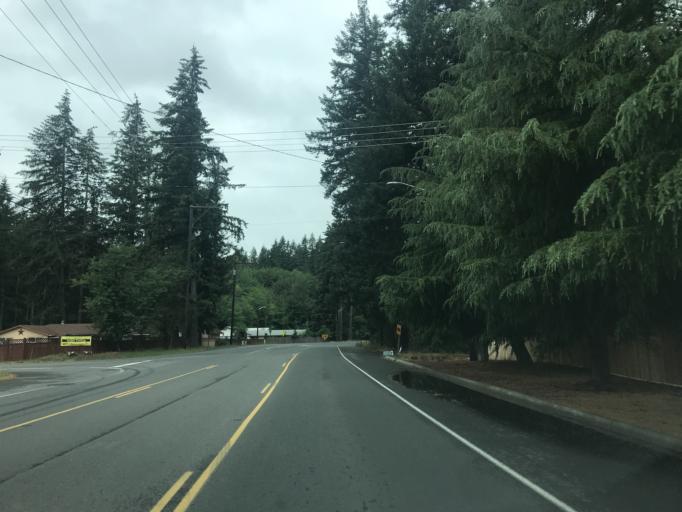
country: US
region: Washington
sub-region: King County
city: Lake Morton-Berrydale
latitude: 47.3436
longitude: -122.1014
